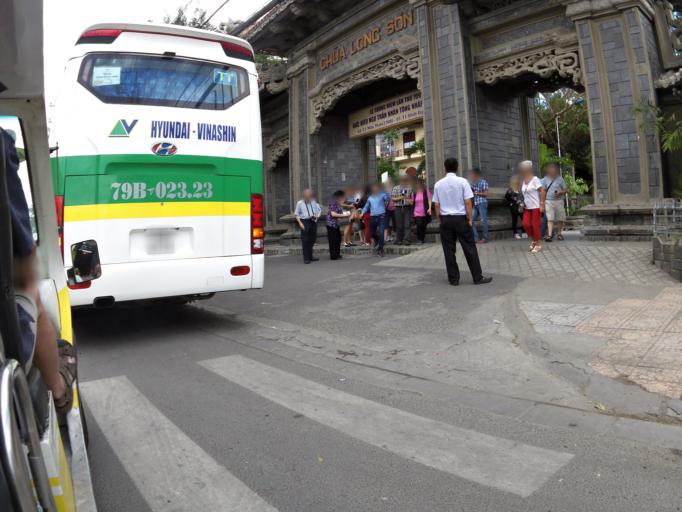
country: VN
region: Khanh Hoa
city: Nha Trang
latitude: 12.2501
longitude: 109.1802
